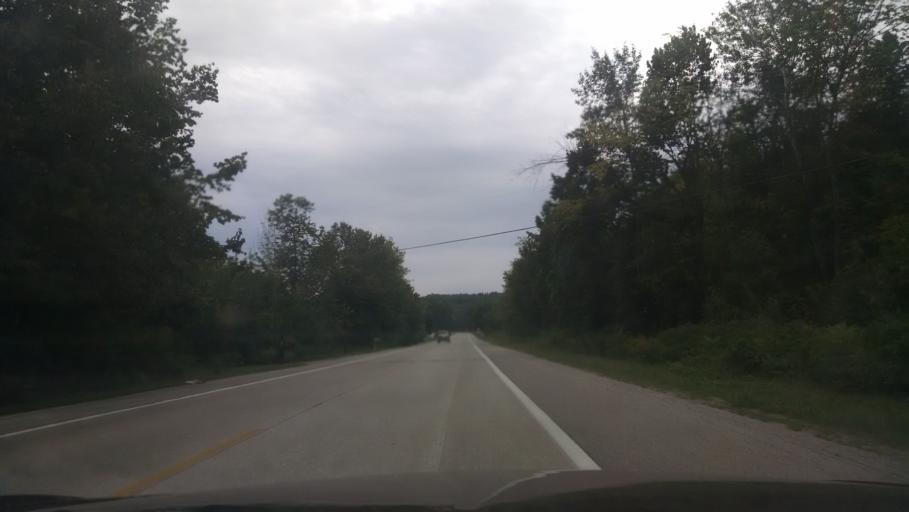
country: US
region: Michigan
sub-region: Leelanau County
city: Greilickville
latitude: 44.8776
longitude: -85.6493
